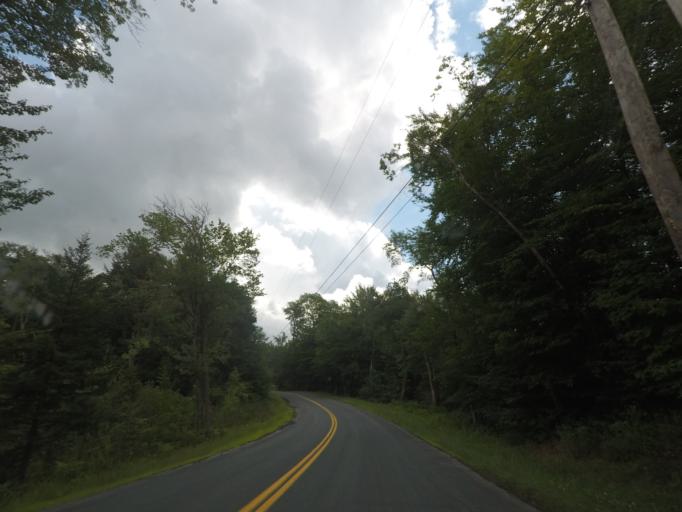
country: US
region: New York
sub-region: Rensselaer County
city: Averill Park
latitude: 42.6665
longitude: -73.4168
